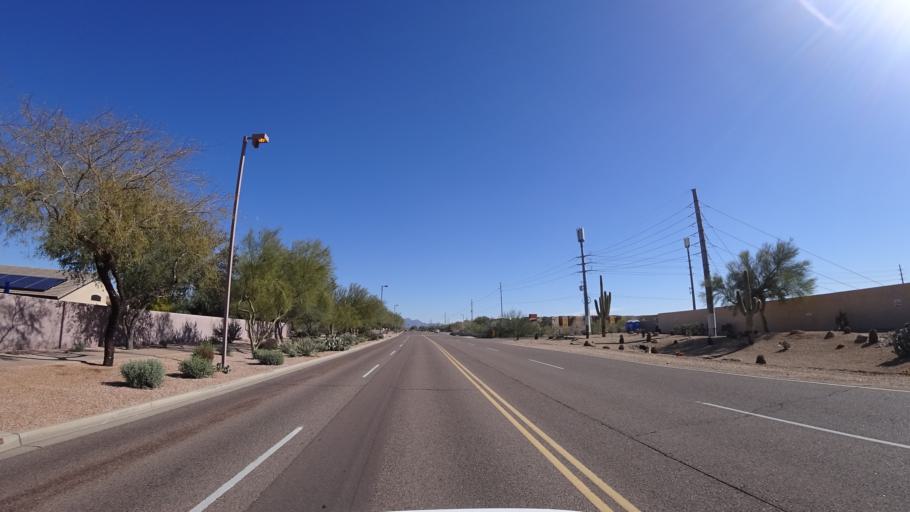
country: US
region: Arizona
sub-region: Maricopa County
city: Carefree
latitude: 33.6815
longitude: -111.9808
